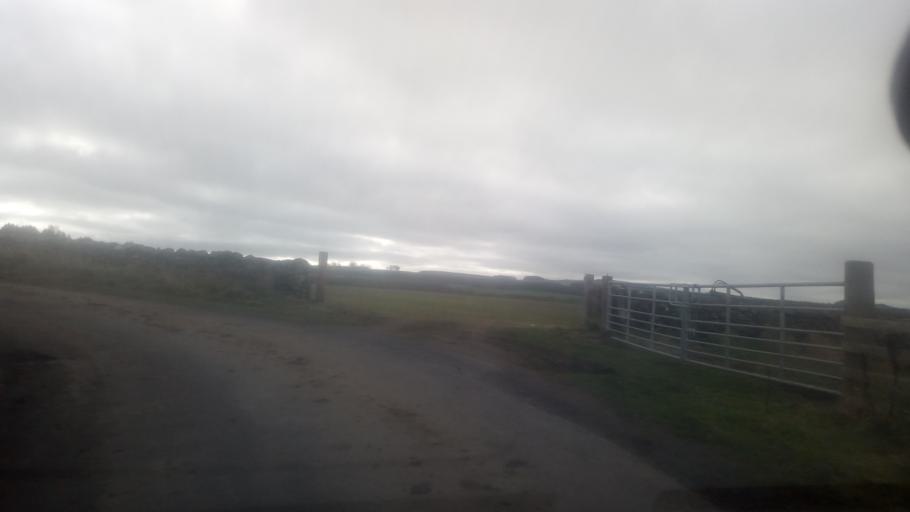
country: GB
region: Scotland
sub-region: The Scottish Borders
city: Kelso
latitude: 55.5669
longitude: -2.5107
